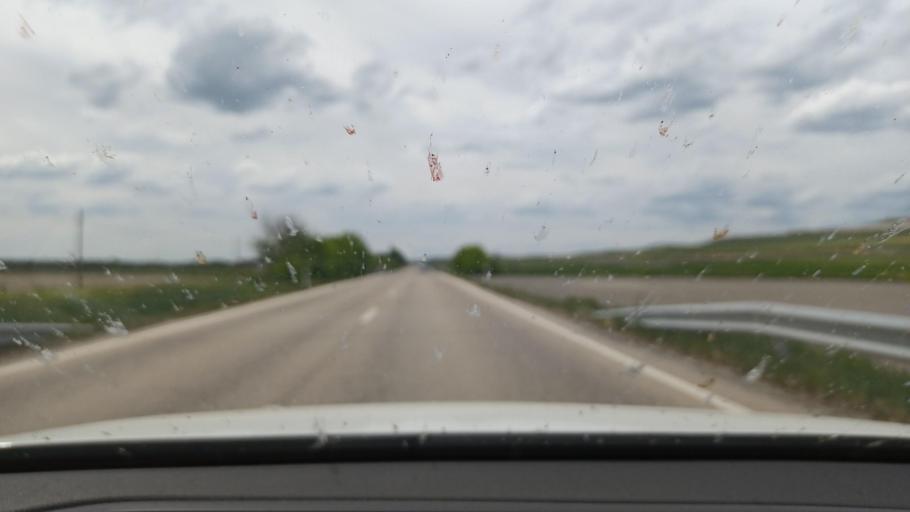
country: ES
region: Castille and Leon
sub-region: Provincia de Segovia
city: Cuellar
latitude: 41.3846
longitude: -4.2527
